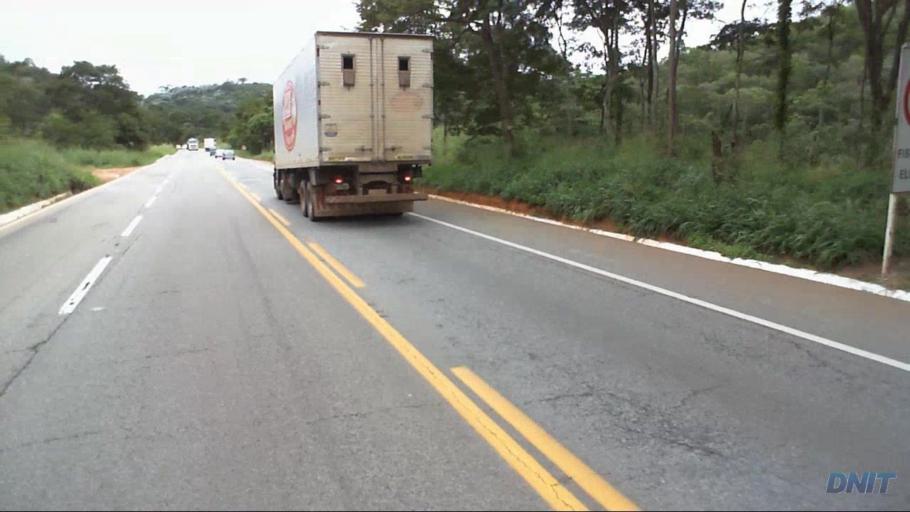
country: BR
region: Minas Gerais
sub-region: Barao De Cocais
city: Barao de Cocais
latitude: -19.8007
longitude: -43.4135
